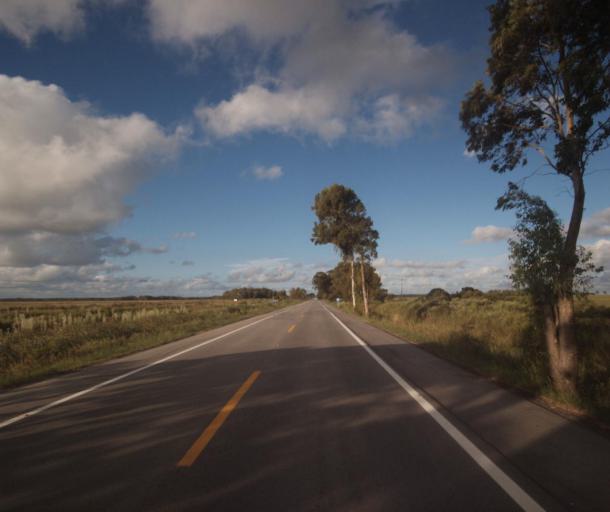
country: BR
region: Rio Grande do Sul
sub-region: Rio Grande
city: Rio Grande
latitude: -32.1372
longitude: -52.3770
